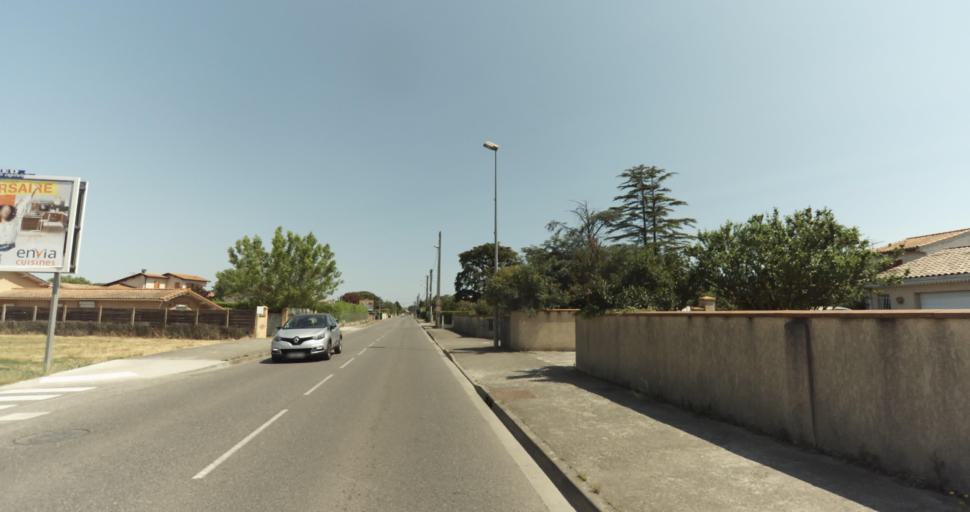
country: FR
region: Midi-Pyrenees
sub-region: Departement de la Haute-Garonne
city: La Salvetat-Saint-Gilles
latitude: 43.5697
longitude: 1.2674
